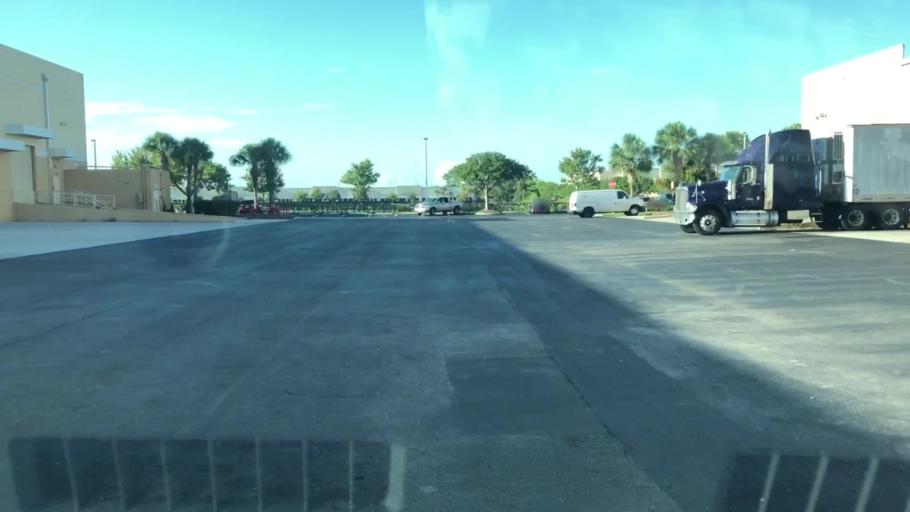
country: US
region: Florida
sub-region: Miami-Dade County
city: Country Club
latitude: 25.9759
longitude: -80.3008
